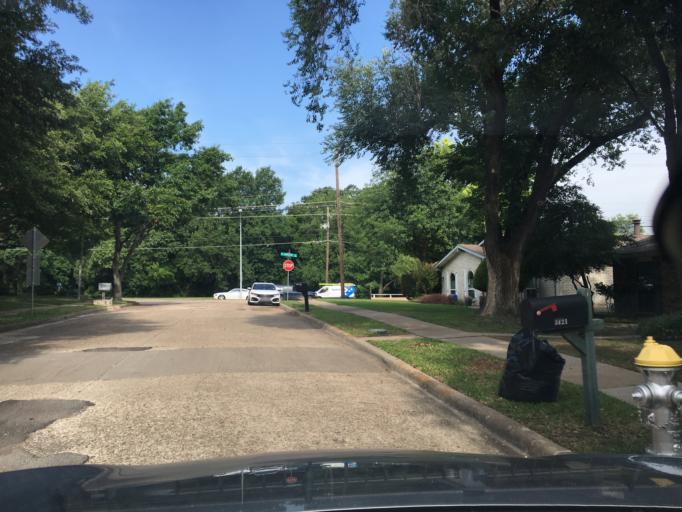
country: US
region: Texas
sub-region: Dallas County
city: Richardson
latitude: 32.9700
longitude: -96.6819
